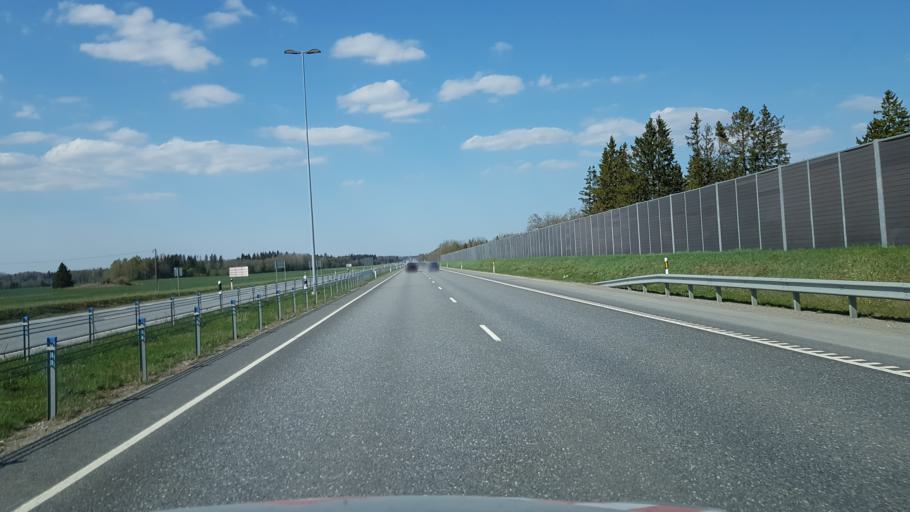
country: EE
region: Harju
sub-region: Rae vald
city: Vaida
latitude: 59.2029
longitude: 25.0405
